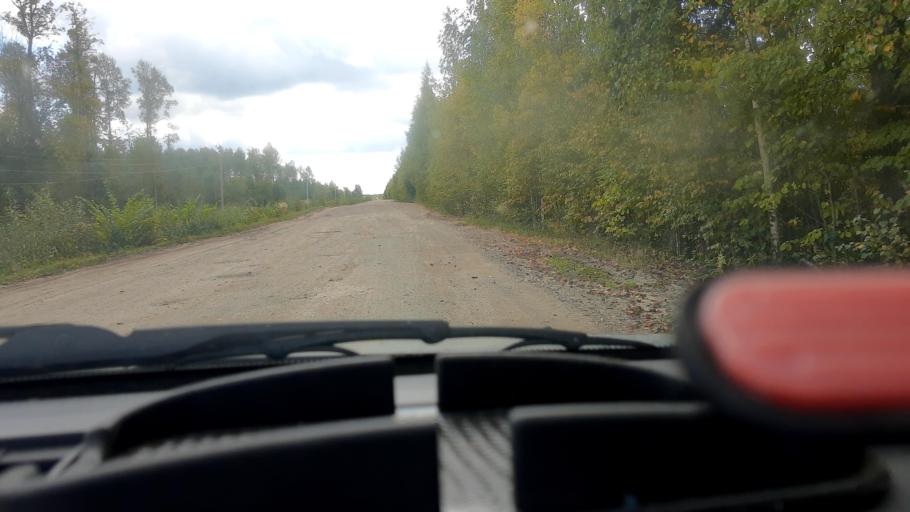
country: RU
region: Mariy-El
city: Kilemary
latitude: 56.8953
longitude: 46.7500
